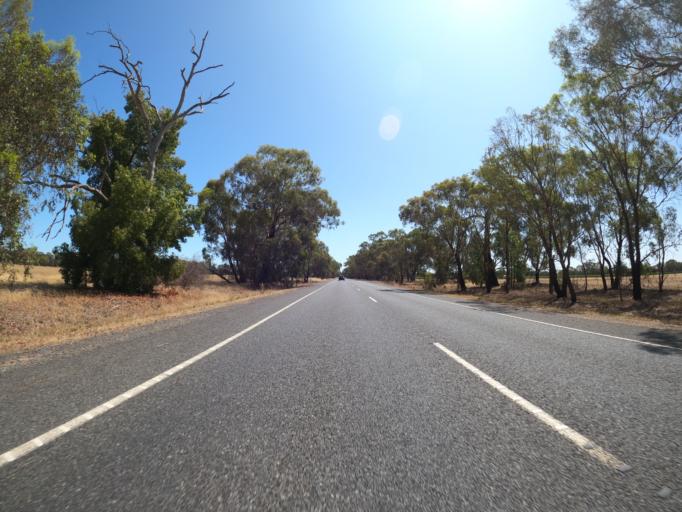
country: AU
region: New South Wales
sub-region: Corowa Shire
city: Corowa
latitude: -36.0623
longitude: 146.4029
